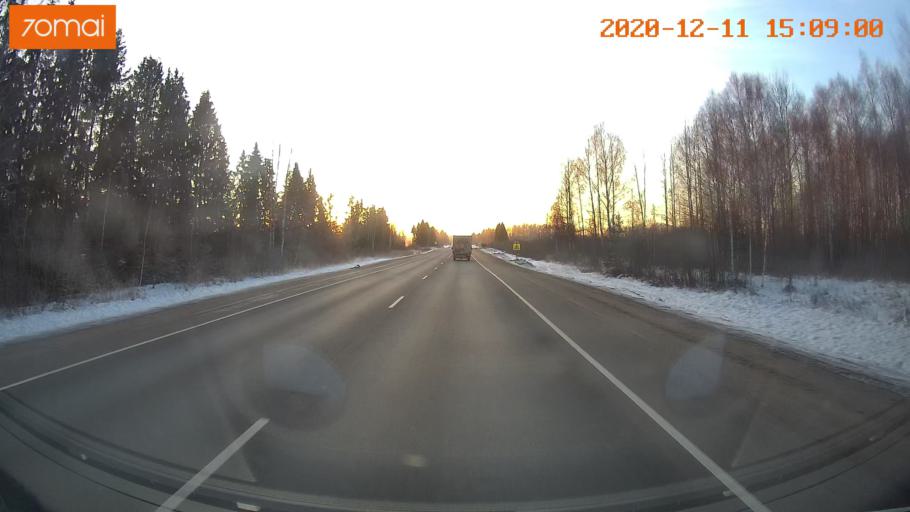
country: RU
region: Ivanovo
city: Furmanov
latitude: 57.2949
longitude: 41.1825
